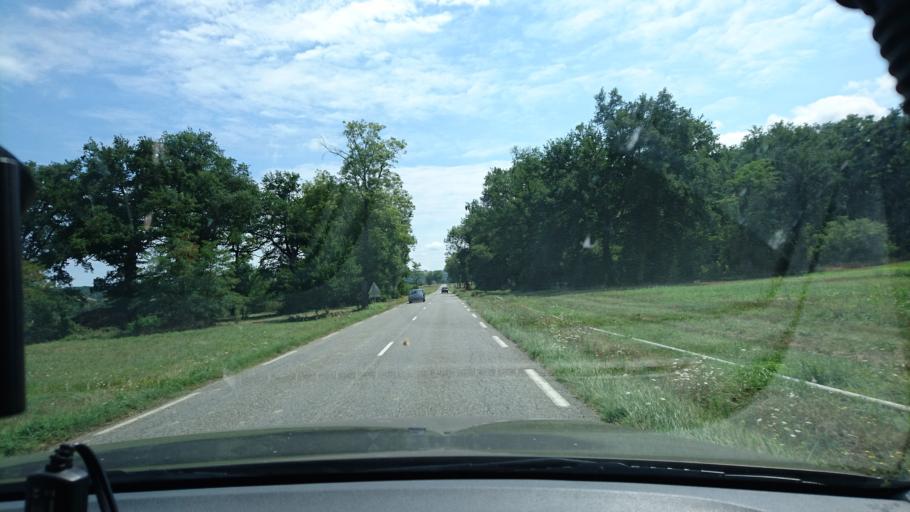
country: FR
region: Midi-Pyrenees
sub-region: Departement de la Haute-Garonne
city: Gaillac-Toulza
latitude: 43.1582
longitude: 1.4231
